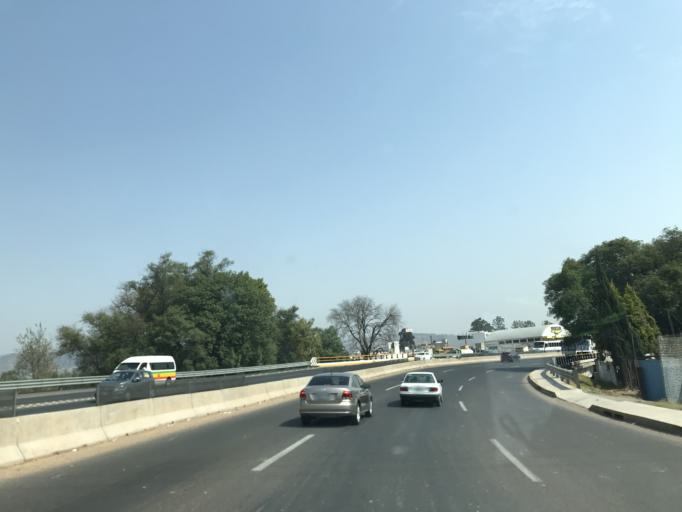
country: MX
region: Tlaxcala
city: Tlaxcala de Xicohtencatl
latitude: 19.3142
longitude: -98.2046
